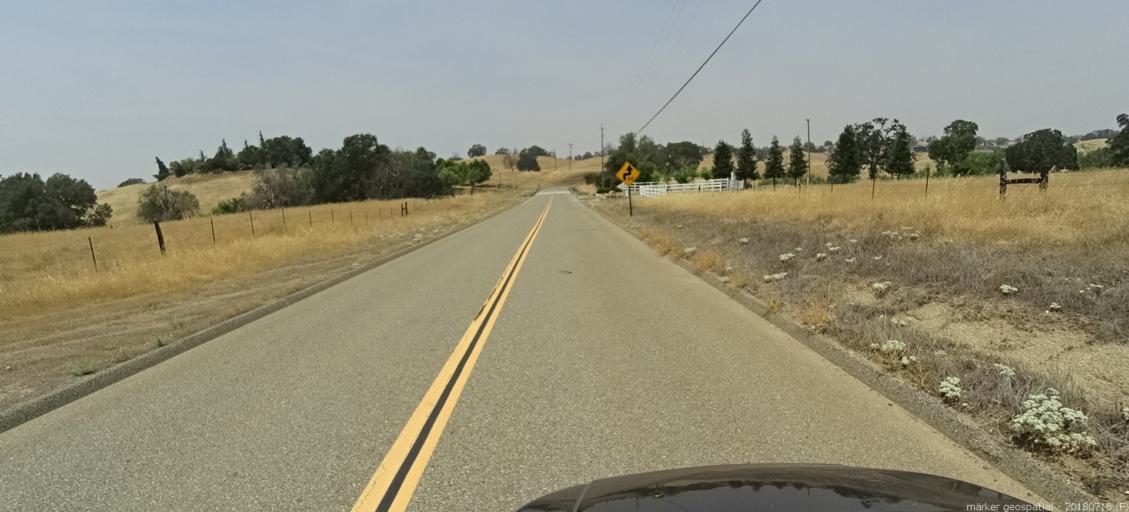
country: US
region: California
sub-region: Madera County
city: Yosemite Lakes
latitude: 37.1339
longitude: -119.8997
